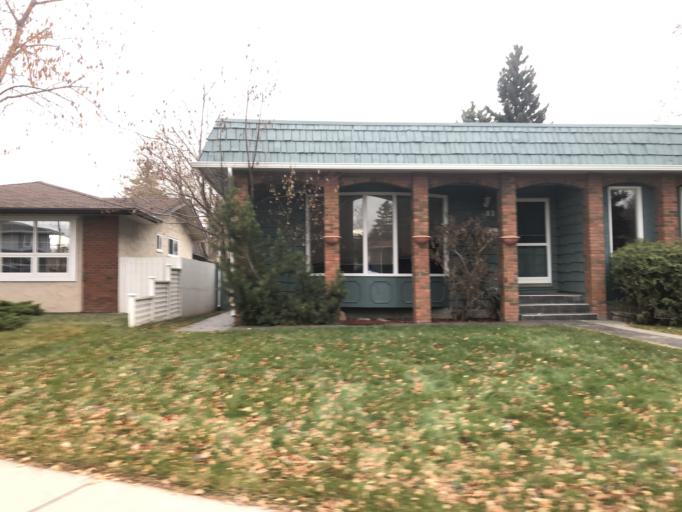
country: CA
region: Alberta
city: Calgary
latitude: 50.9394
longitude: -114.0409
